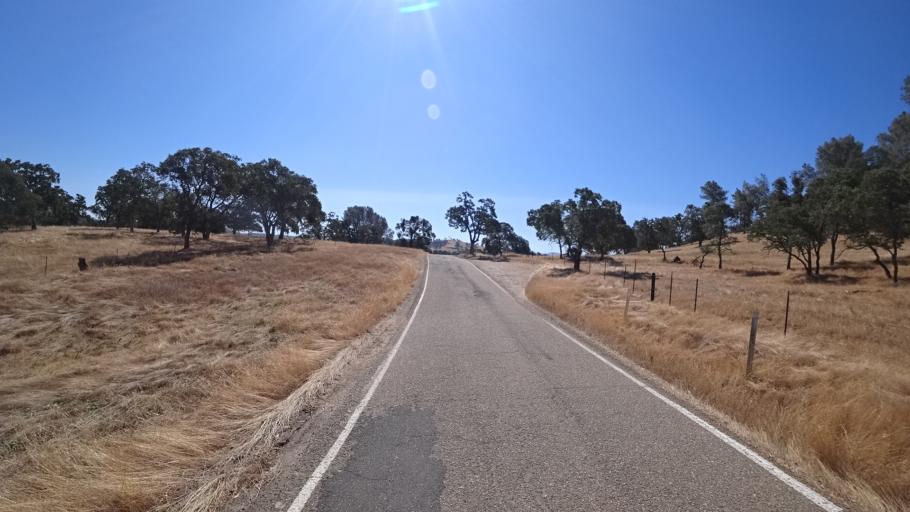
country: US
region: California
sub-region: Calaveras County
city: Valley Springs
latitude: 38.2289
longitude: -120.8297
